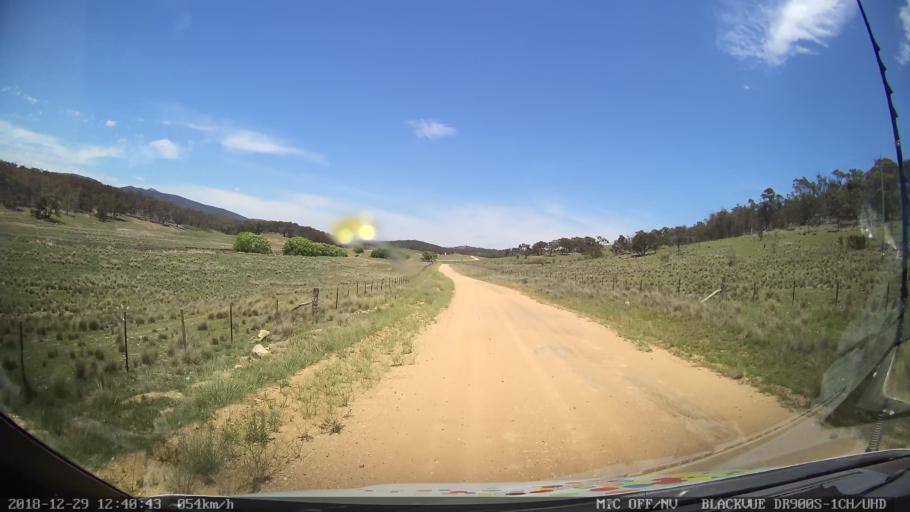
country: AU
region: Australian Capital Territory
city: Macarthur
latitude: -35.6034
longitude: 149.2240
